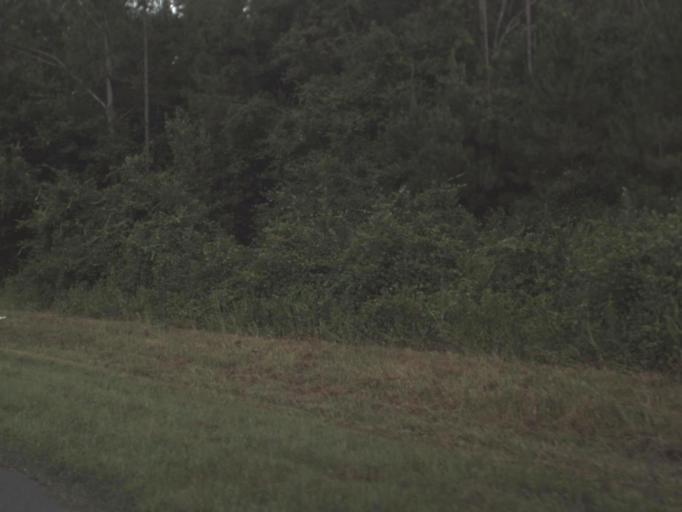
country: US
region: Florida
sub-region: Columbia County
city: Five Points
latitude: 30.3347
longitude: -82.6253
